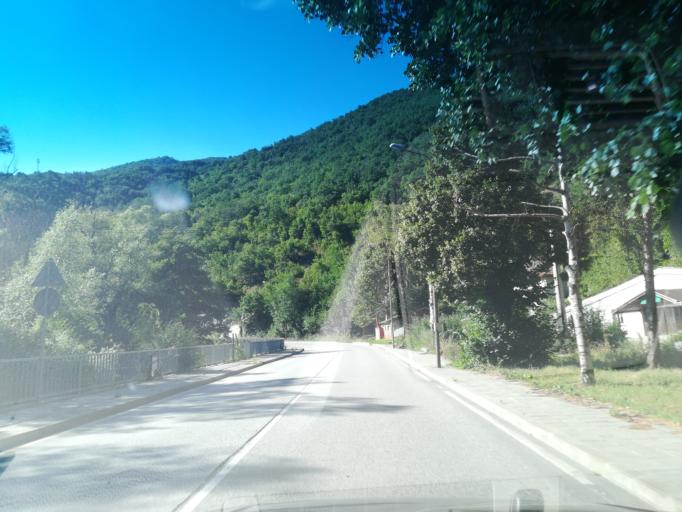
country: BG
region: Plovdiv
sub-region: Obshtina Luki
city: Luki
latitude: 41.8995
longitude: 24.7406
